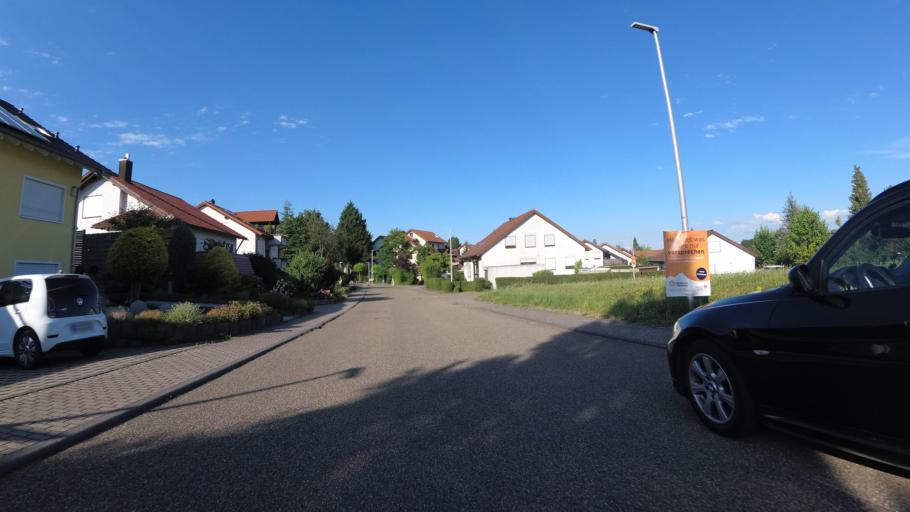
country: DE
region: Baden-Wuerttemberg
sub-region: Regierungsbezirk Stuttgart
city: Bad Wimpfen
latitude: 49.2265
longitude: 9.1528
